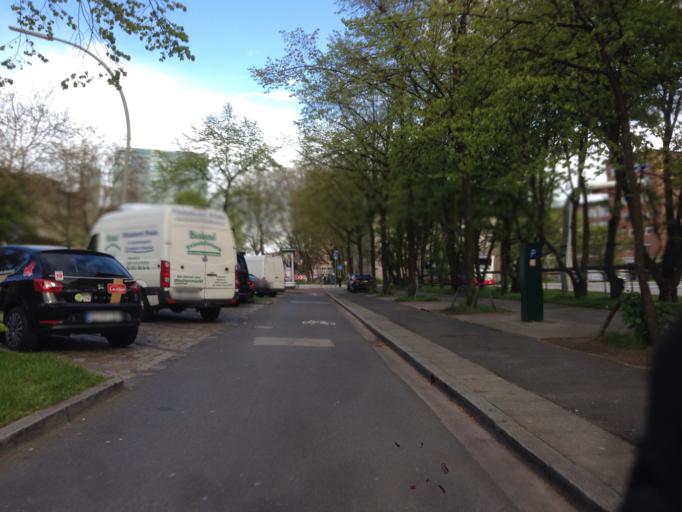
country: DE
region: Hamburg
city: Hamburg-Mitte
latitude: 53.5524
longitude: 10.0144
